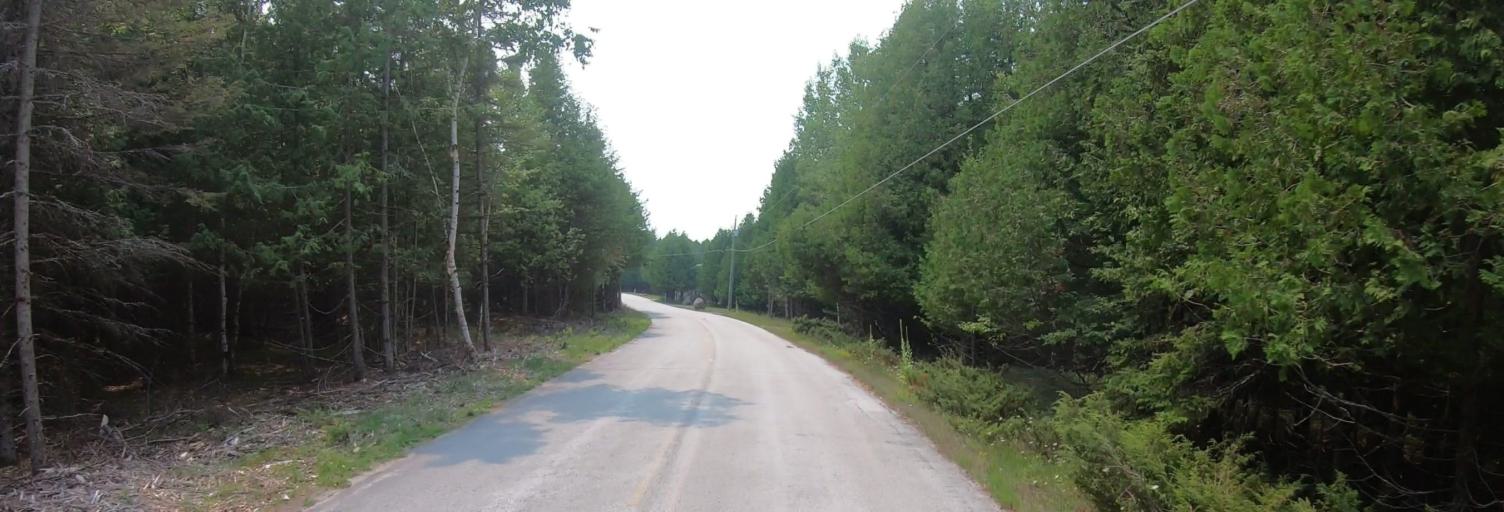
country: CA
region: Ontario
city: Thessalon
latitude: 46.0247
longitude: -83.7620
